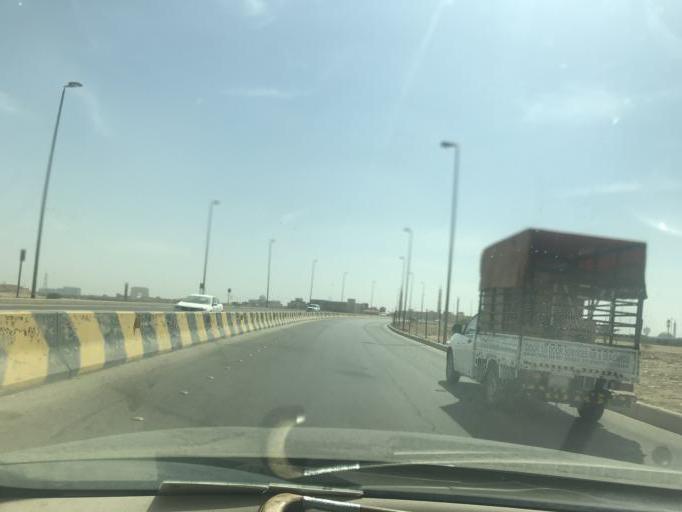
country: SA
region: Ar Riyad
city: Riyadh
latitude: 24.8251
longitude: 46.7211
